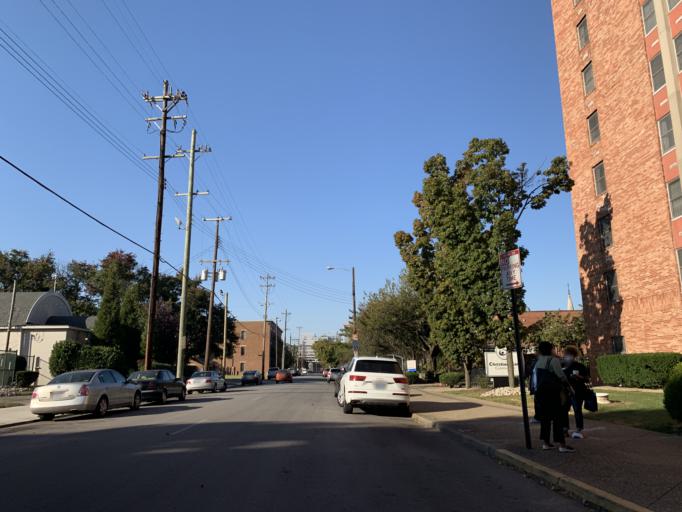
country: US
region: Kentucky
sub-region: Jefferson County
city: Louisville
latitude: 38.2402
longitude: -85.7606
